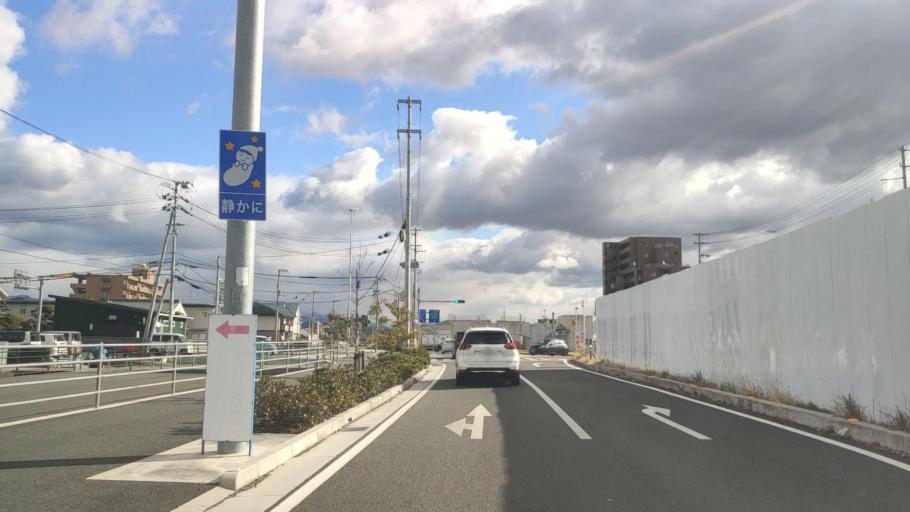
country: JP
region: Ehime
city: Masaki-cho
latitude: 33.8114
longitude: 132.7258
